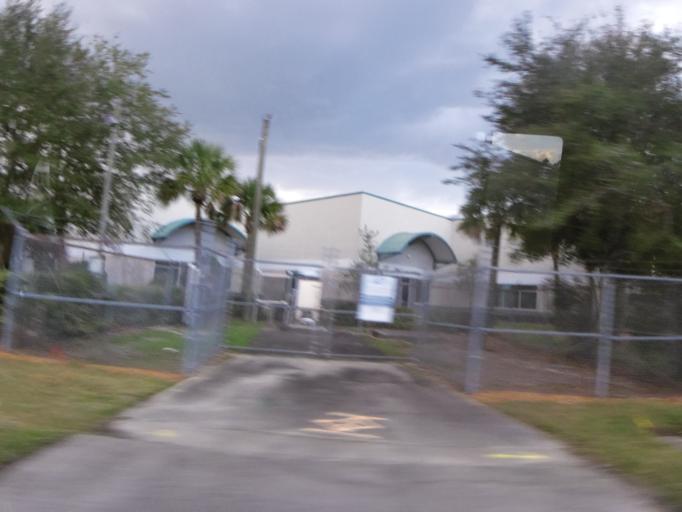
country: US
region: Florida
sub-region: Saint Johns County
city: Fruit Cove
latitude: 30.1857
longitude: -81.5736
